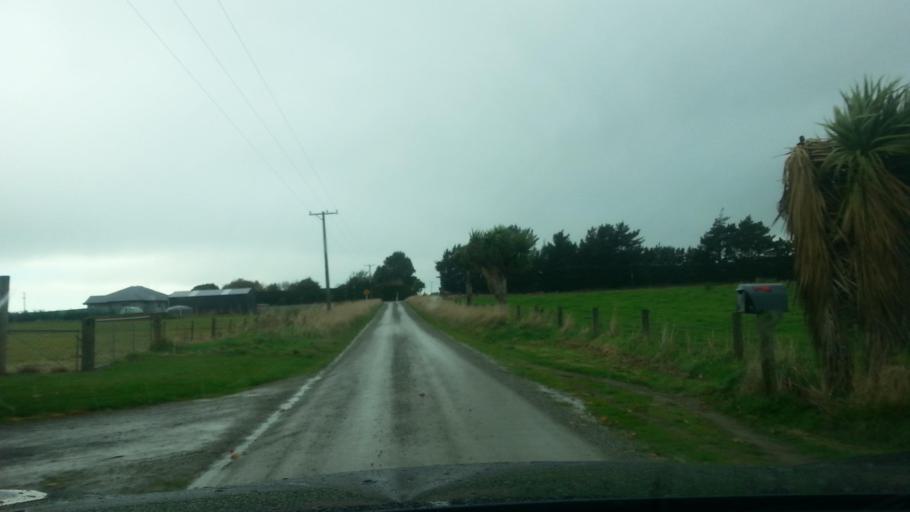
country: NZ
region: Southland
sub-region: Invercargill City
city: Invercargill
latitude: -46.3387
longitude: 168.4130
